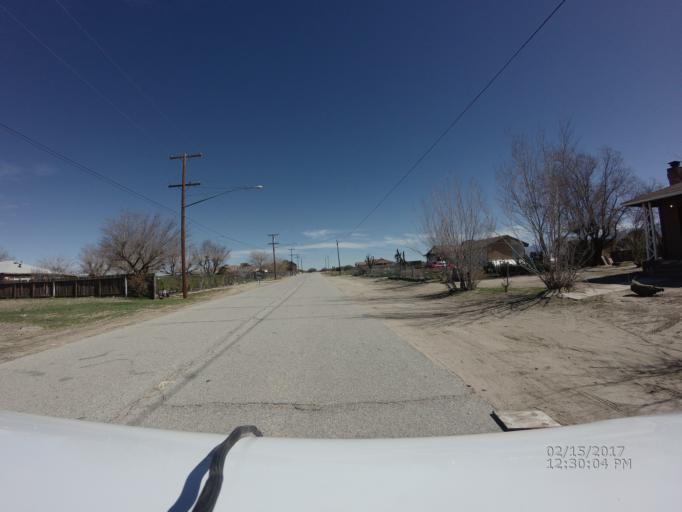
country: US
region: California
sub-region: Los Angeles County
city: Littlerock
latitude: 34.5853
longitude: -117.9538
